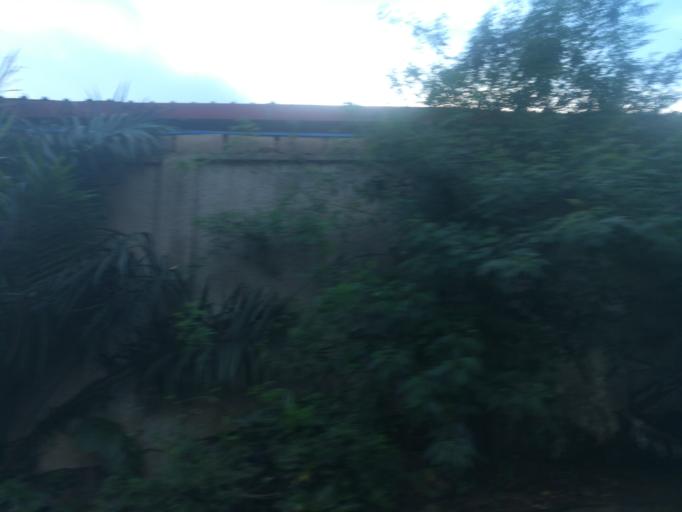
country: NG
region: Lagos
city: Somolu
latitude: 6.5615
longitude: 3.3725
